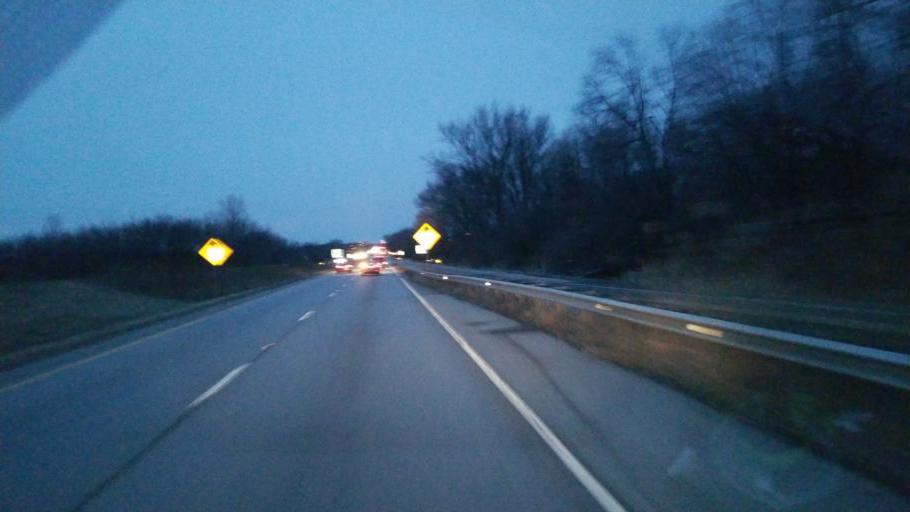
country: US
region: Illinois
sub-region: Lake County
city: Wadsworth
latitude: 42.4744
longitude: -87.9474
